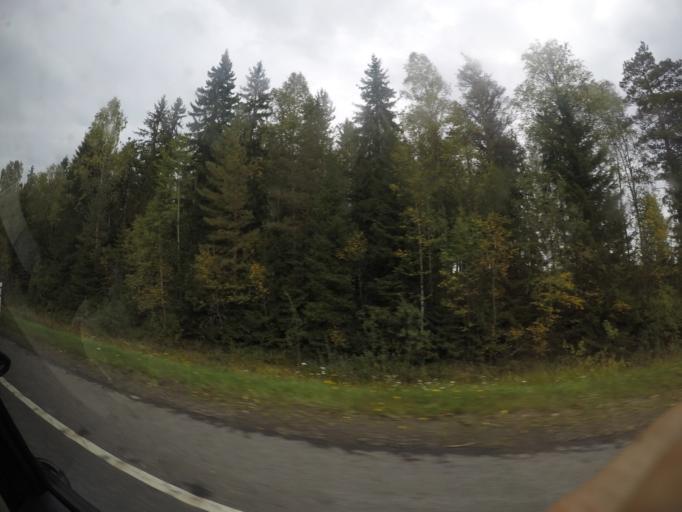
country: FI
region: Haeme
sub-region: Haemeenlinna
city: Parola
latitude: 61.1422
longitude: 24.4144
